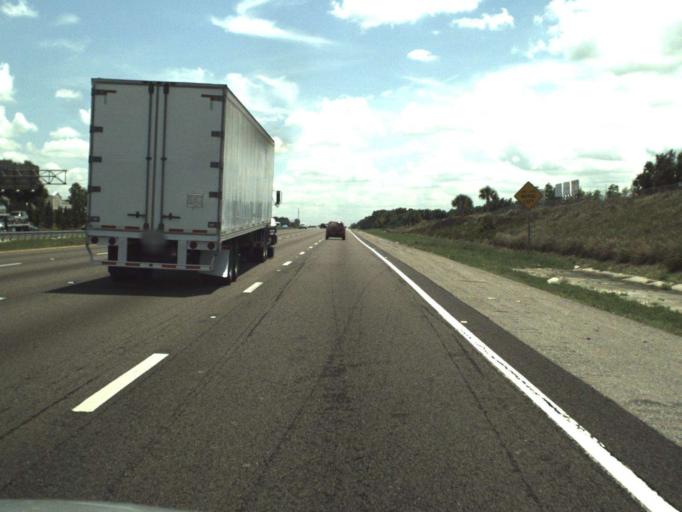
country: US
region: Florida
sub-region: Seminole County
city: Heathrow
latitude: 28.7491
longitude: -81.3661
